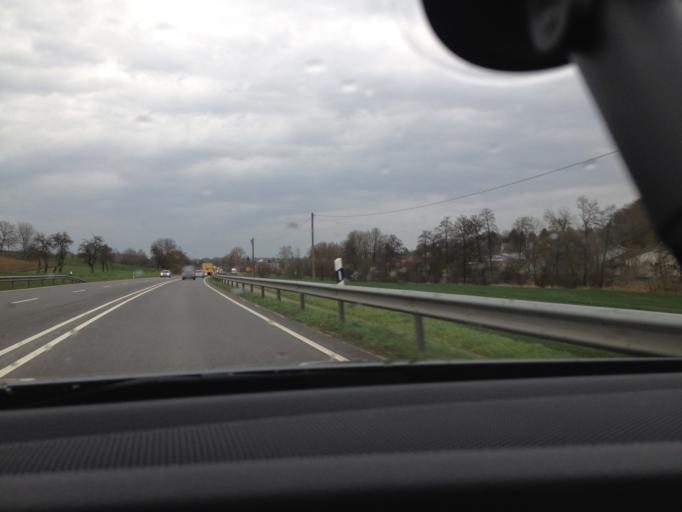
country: DE
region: Baden-Wuerttemberg
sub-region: Karlsruhe Region
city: Aglasterhausen
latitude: 49.3467
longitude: 8.9799
